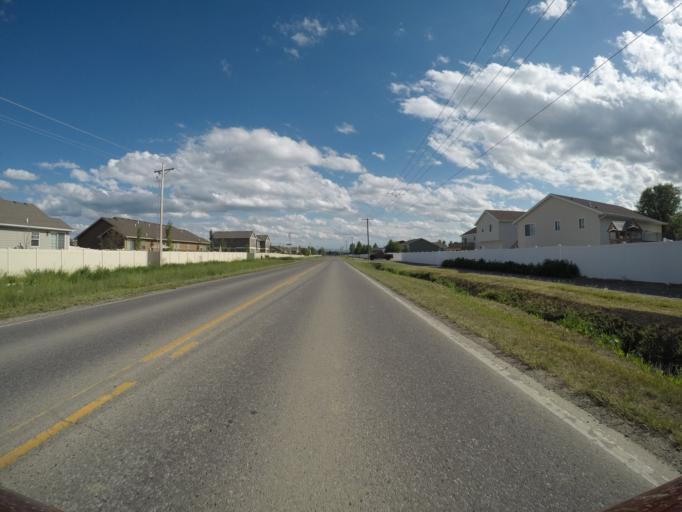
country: US
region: Montana
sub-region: Yellowstone County
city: Billings
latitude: 45.7892
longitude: -108.6527
